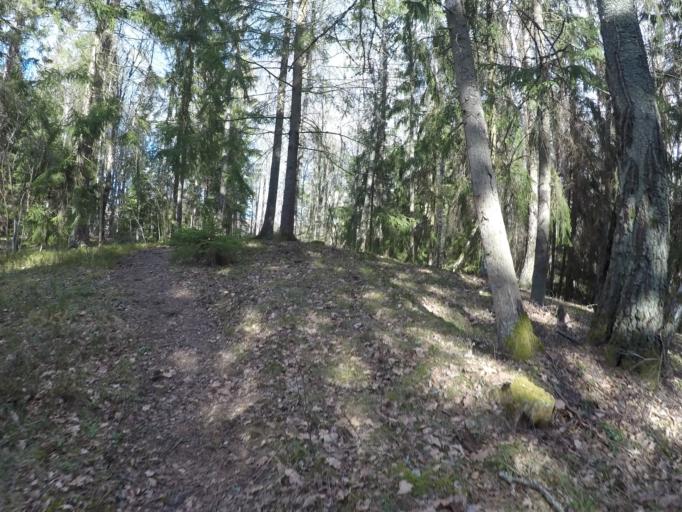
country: SE
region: Soedermanland
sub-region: Eskilstuna Kommun
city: Kvicksund
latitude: 59.4926
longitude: 16.2804
